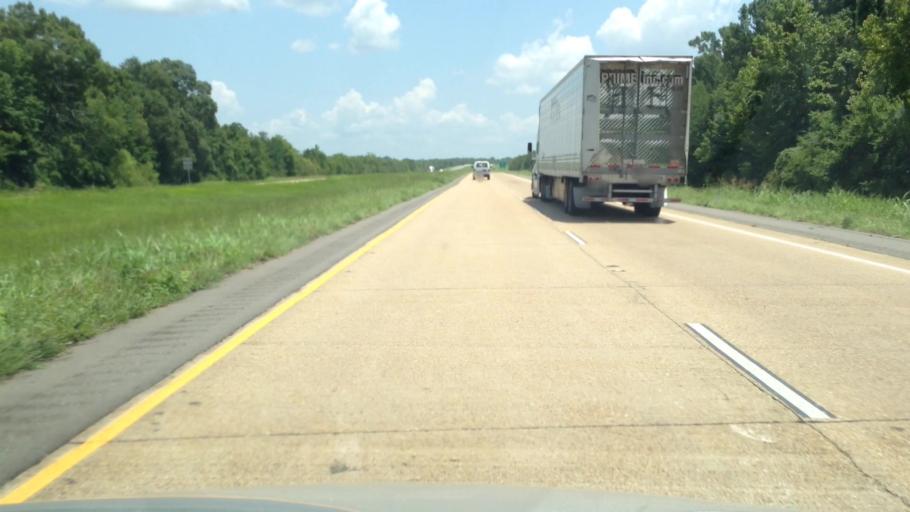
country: US
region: Louisiana
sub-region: Rapides Parish
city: Lecompte
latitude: 30.9926
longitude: -92.3208
